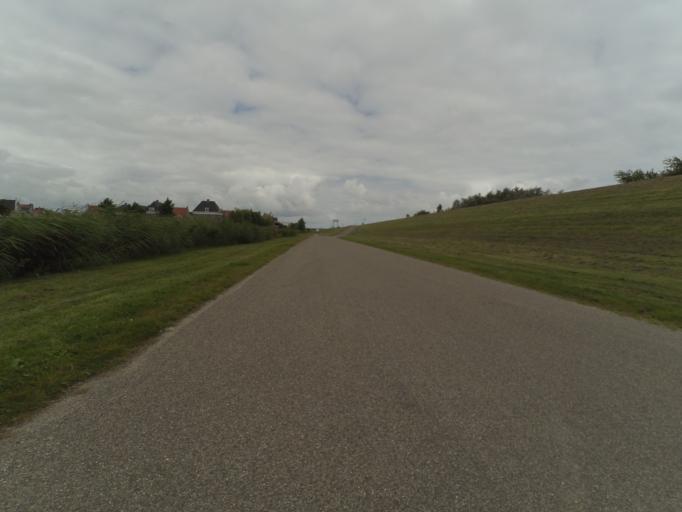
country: NL
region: Friesland
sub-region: Gemeente Dongeradeel
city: Anjum
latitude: 53.3753
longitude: 6.1618
